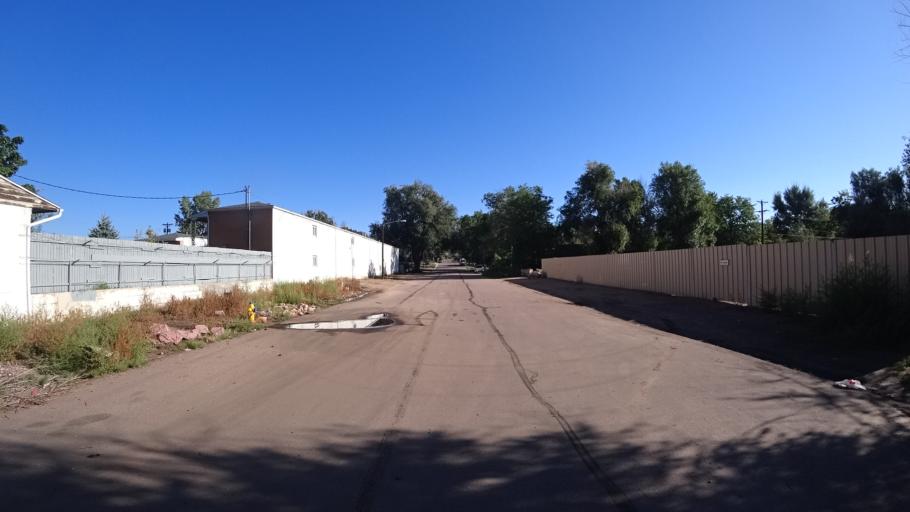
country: US
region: Colorado
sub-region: El Paso County
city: Colorado Springs
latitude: 38.8172
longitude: -104.8208
